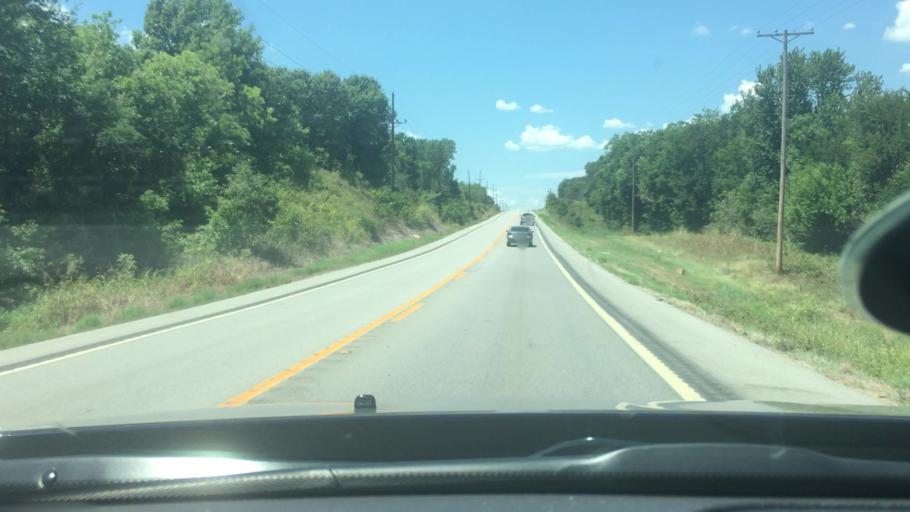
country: US
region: Oklahoma
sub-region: Bryan County
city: Durant
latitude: 33.9974
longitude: -96.2567
